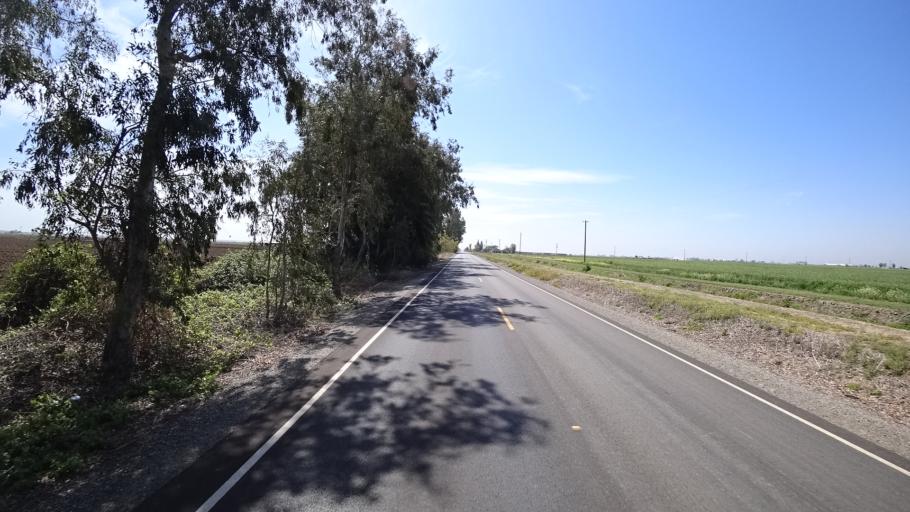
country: US
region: California
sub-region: Glenn County
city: Willows
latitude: 39.5859
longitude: -122.0652
